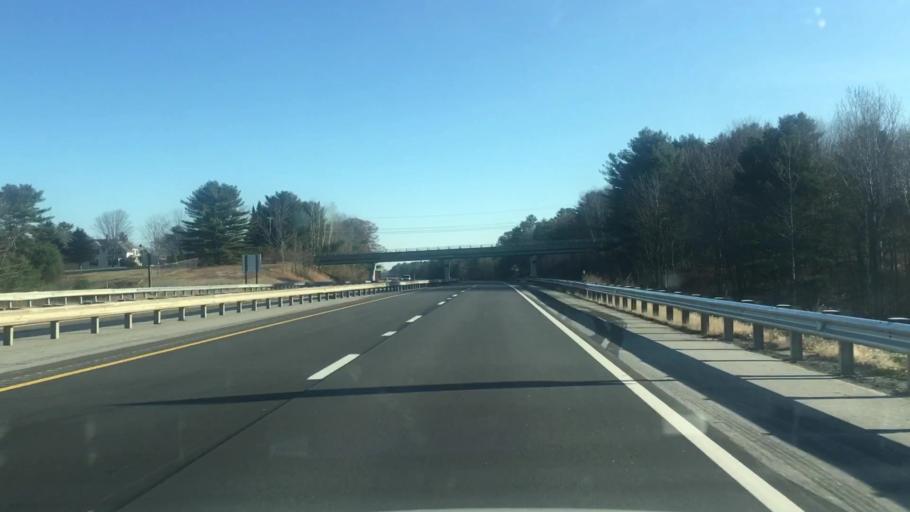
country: US
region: Maine
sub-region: Androscoggin County
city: Auburn
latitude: 44.0400
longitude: -70.2601
